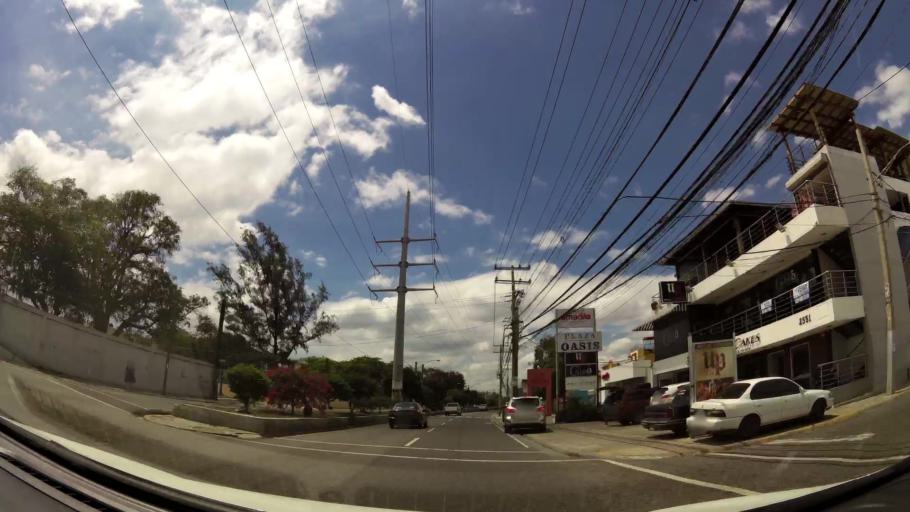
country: DO
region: Nacional
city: Bella Vista
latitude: 18.4393
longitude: -69.9484
